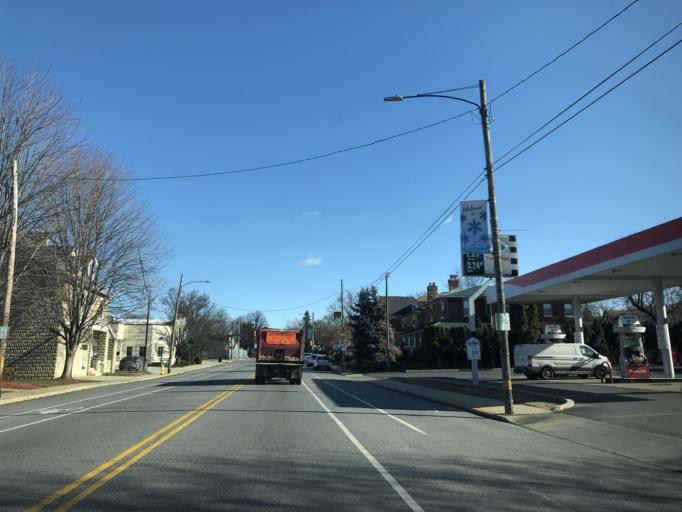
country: US
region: Pennsylvania
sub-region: Chester County
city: Coatesville
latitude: 39.9862
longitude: -75.8058
